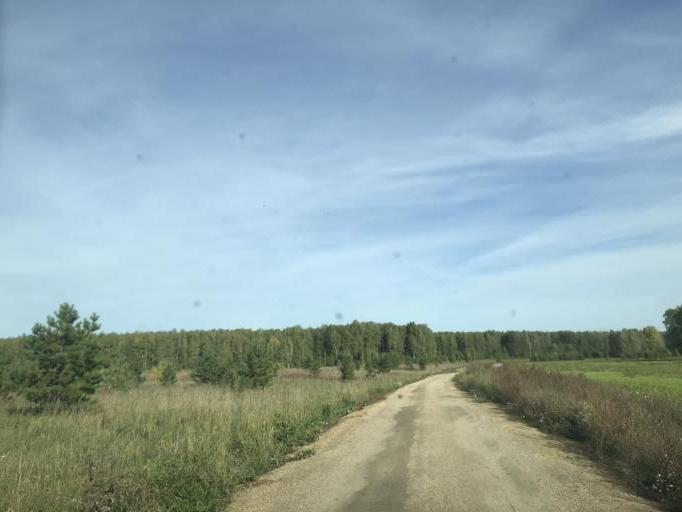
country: RU
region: Chelyabinsk
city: Poletayevo
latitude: 54.9803
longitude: 60.9639
